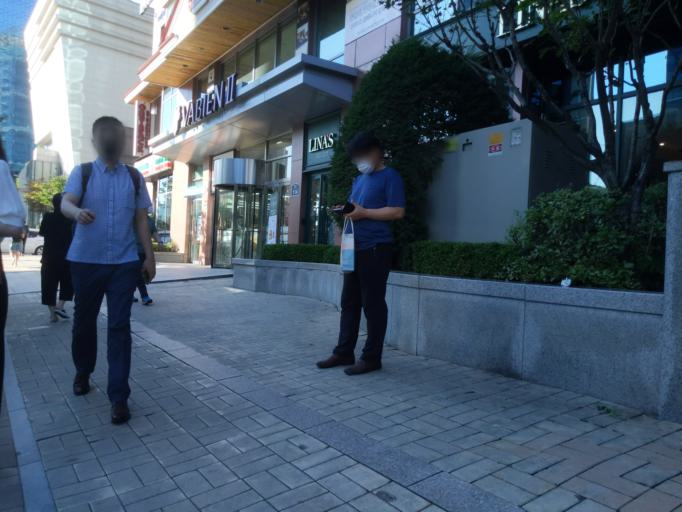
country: KR
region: Seoul
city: Seoul
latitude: 37.5649
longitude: 126.9678
